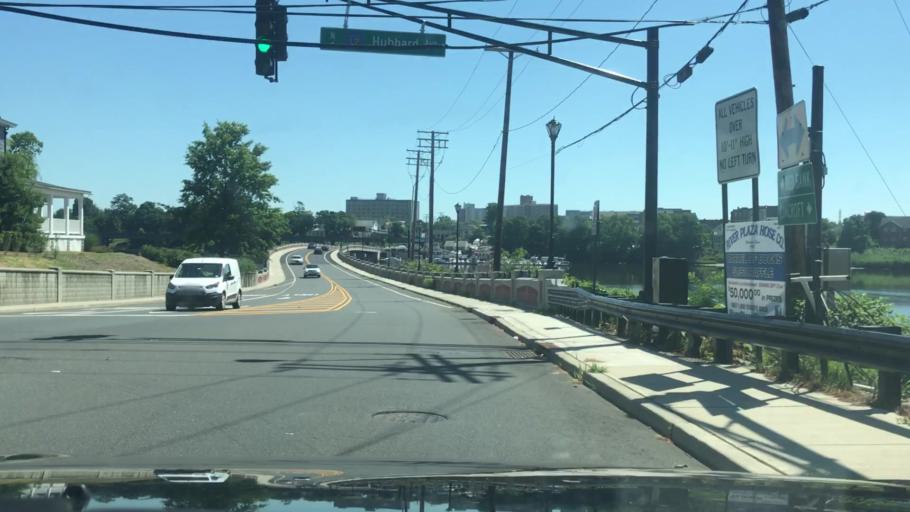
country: US
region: New Jersey
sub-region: Monmouth County
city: Red Bank
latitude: 40.3496
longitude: -74.0816
